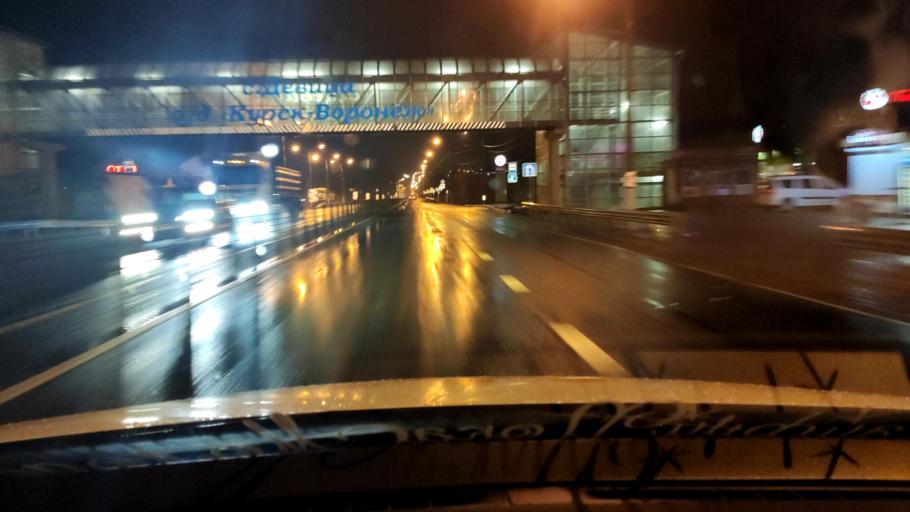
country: RU
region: Voronezj
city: Devitsa
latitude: 51.6346
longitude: 38.9478
